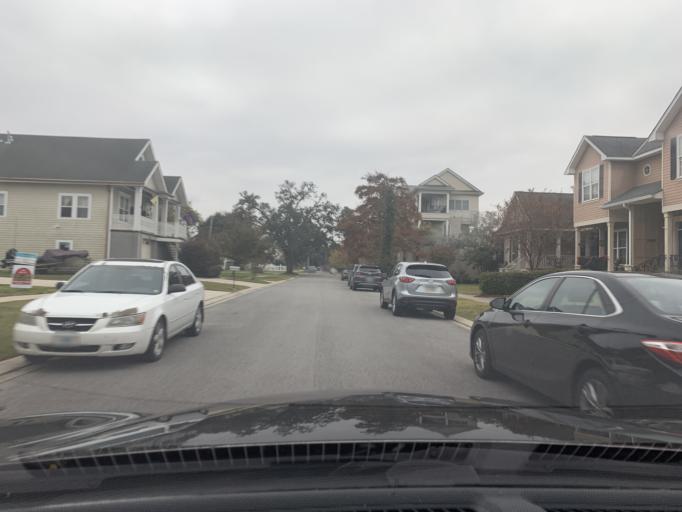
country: US
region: Louisiana
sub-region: Jefferson Parish
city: Metairie
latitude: 30.0134
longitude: -90.1094
